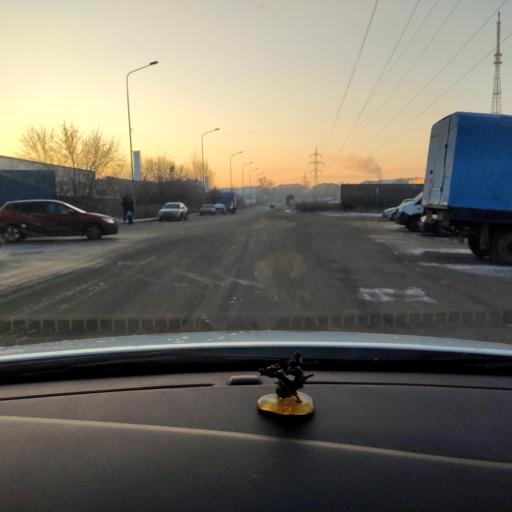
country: RU
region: Tatarstan
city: Staroye Arakchino
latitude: 55.8302
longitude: 49.0301
